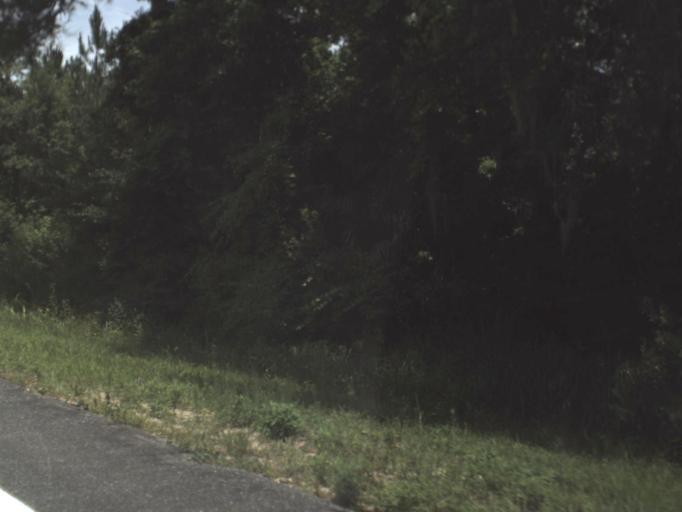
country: US
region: Florida
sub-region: Taylor County
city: Steinhatchee
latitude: 29.8539
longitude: -83.3096
